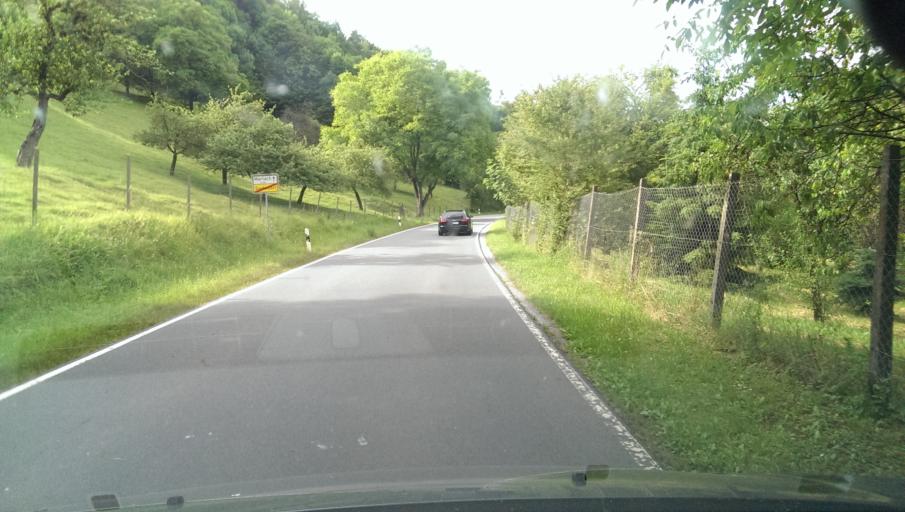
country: DE
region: Baden-Wuerttemberg
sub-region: Regierungsbezirk Stuttgart
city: Krautheim
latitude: 49.3474
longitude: 9.6091
